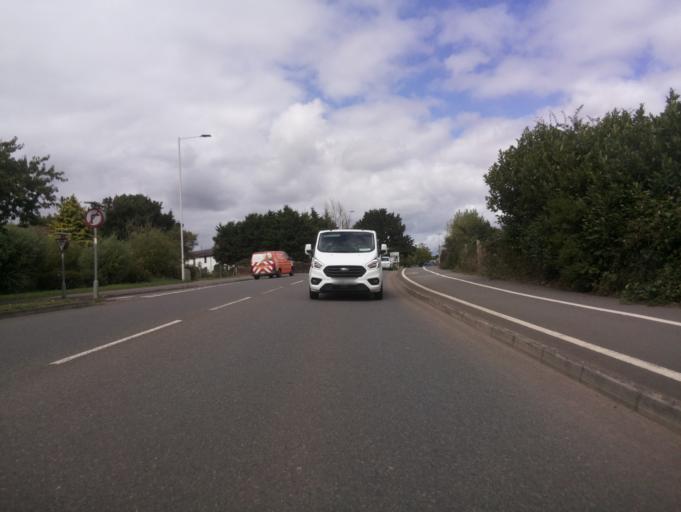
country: GB
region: England
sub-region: Devon
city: Heavitree
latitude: 50.7257
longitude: -3.4826
